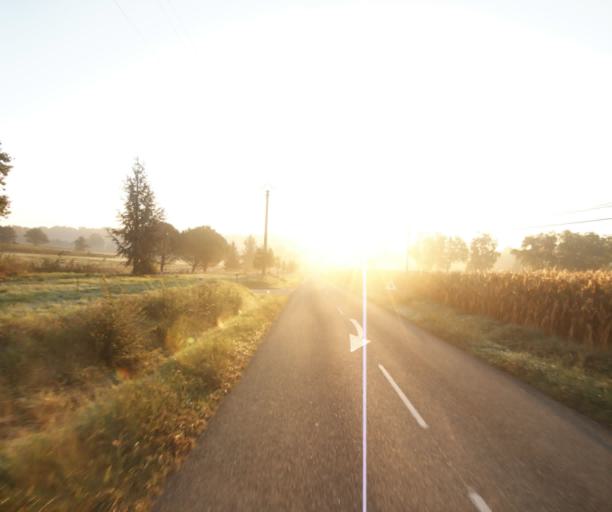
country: FR
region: Midi-Pyrenees
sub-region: Departement du Gers
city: Gondrin
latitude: 43.8166
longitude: 0.1801
